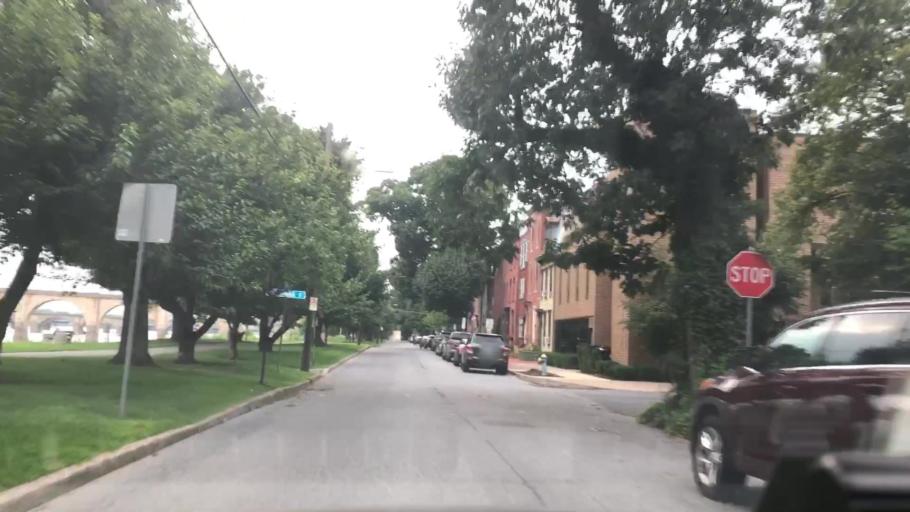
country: US
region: Pennsylvania
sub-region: Cumberland County
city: Lemoyne
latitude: 40.2530
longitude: -76.8750
